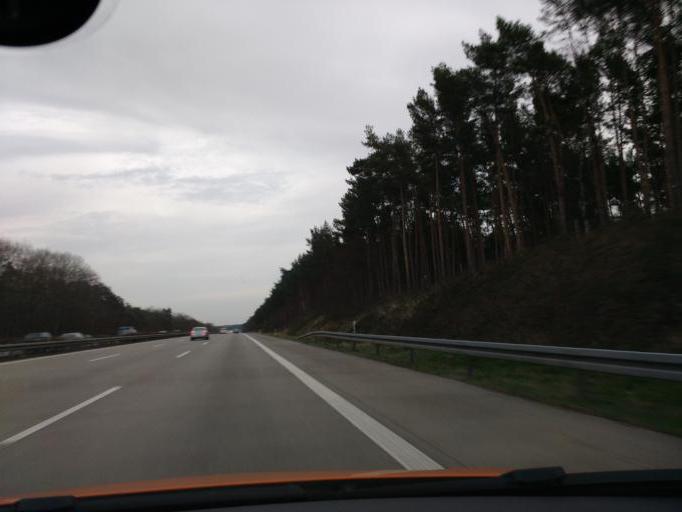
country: DE
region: Saxony-Anhalt
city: Mockern
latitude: 52.2339
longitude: 12.0223
